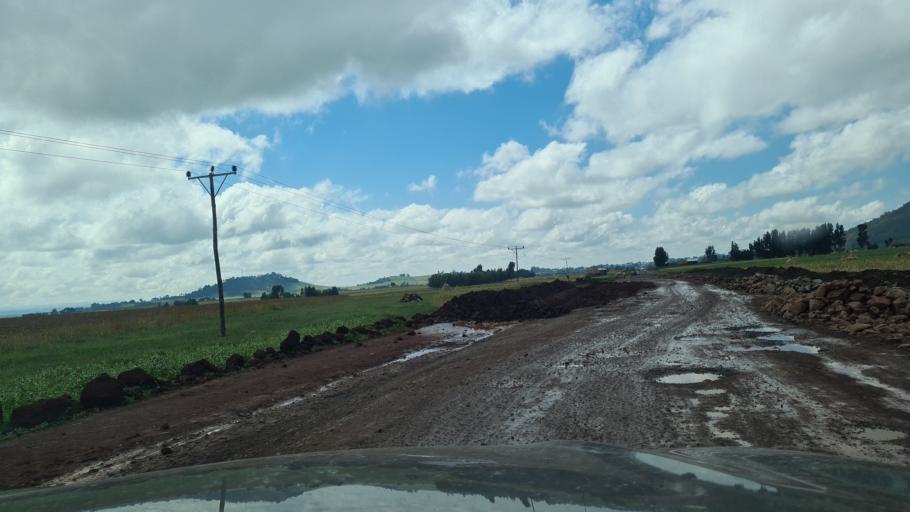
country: ET
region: Oromiya
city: Huruta
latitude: 8.0902
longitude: 39.5383
